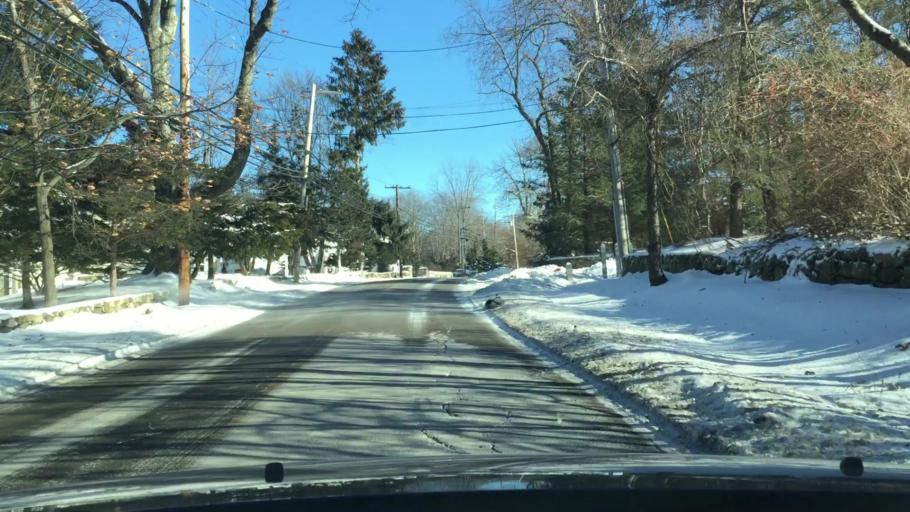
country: US
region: Massachusetts
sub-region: Essex County
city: North Andover
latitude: 42.6865
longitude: -71.1016
